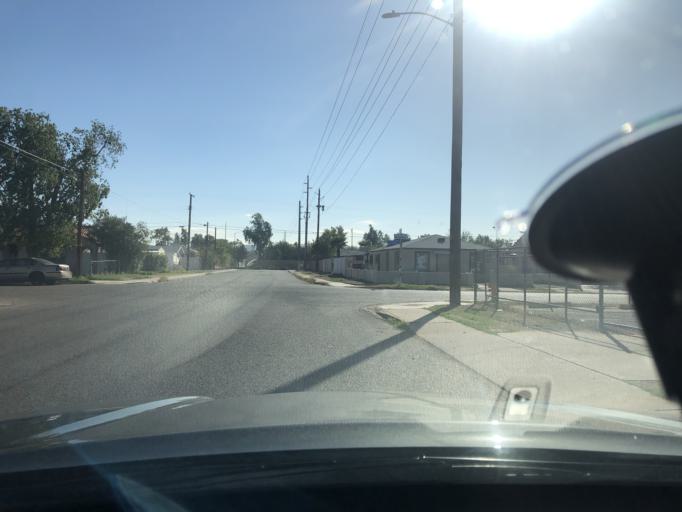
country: US
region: Arizona
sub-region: Maricopa County
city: Phoenix
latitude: 33.4640
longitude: -112.0434
